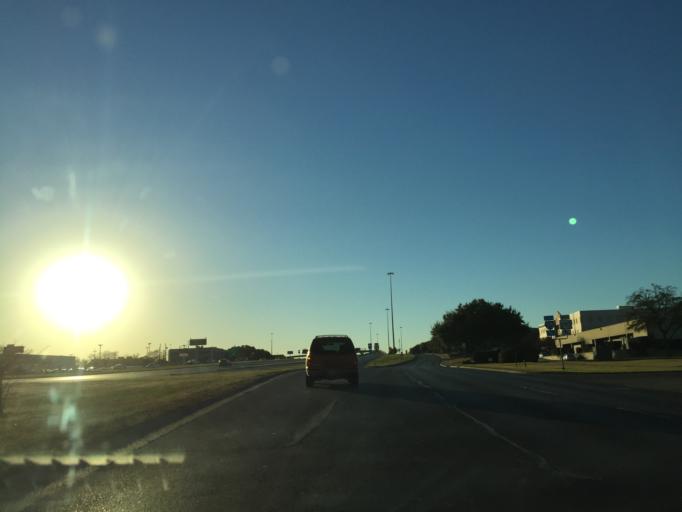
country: US
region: Texas
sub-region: Travis County
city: Austin
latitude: 30.3220
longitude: -97.6964
